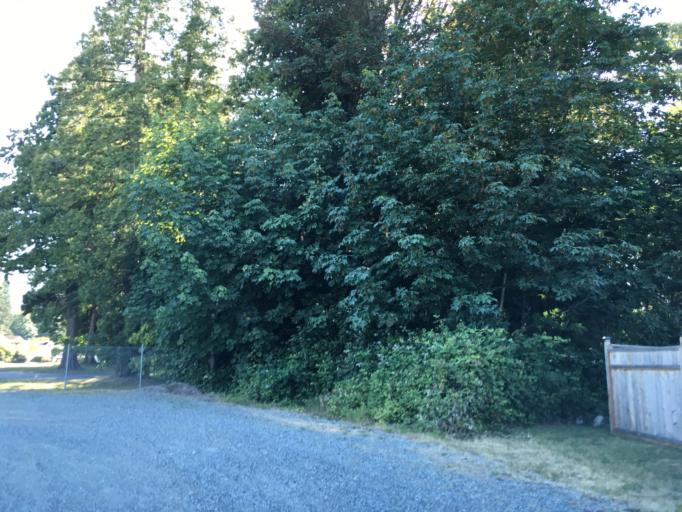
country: US
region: Washington
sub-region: Whatcom County
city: Birch Bay
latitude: 48.9070
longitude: -122.7539
